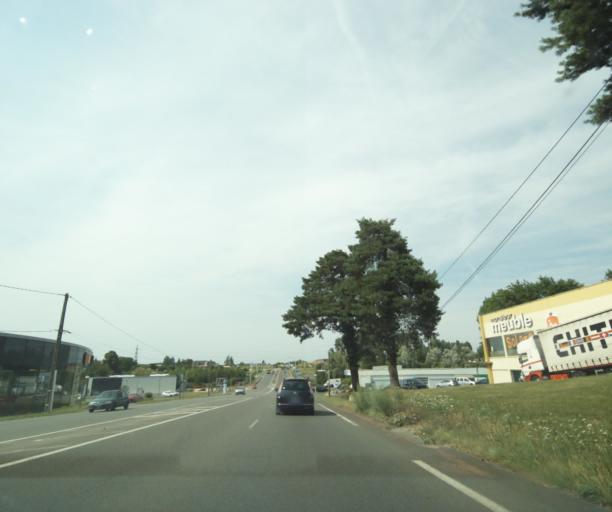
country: FR
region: Centre
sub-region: Departement d'Indre-et-Loire
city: Chambray-les-Tours
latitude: 47.3176
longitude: 0.7108
